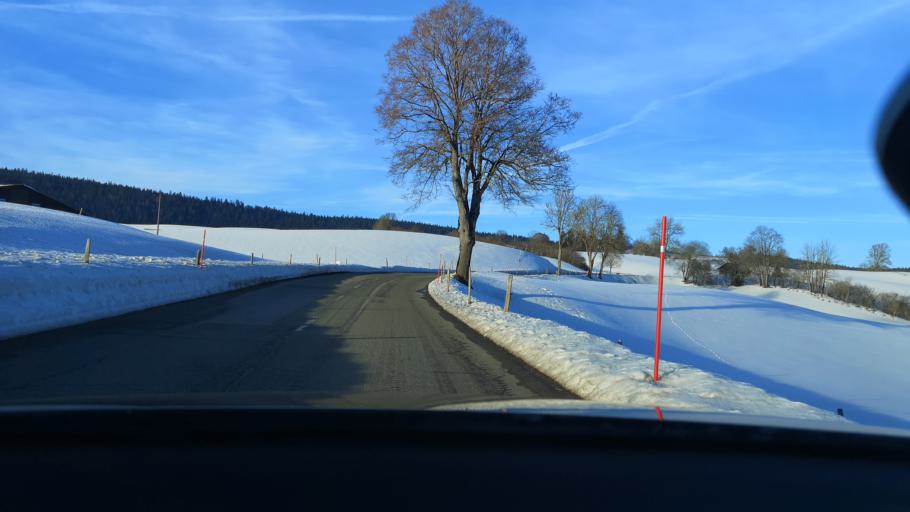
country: CH
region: Neuchatel
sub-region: Val-de-Travers District
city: Fleurier
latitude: 46.9084
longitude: 6.5002
